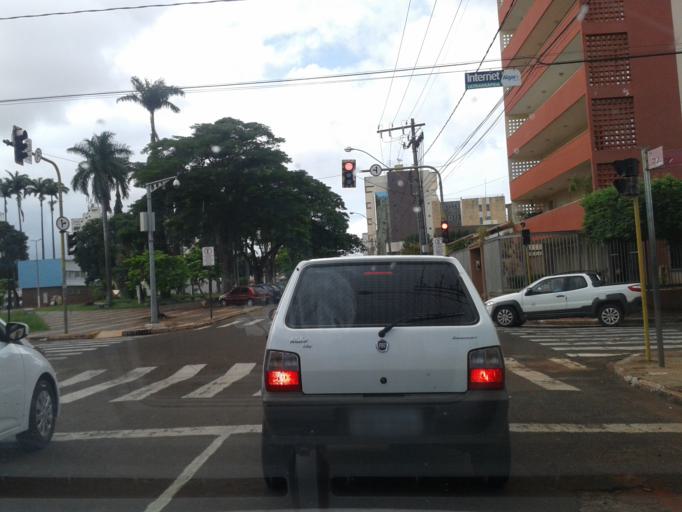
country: BR
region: Minas Gerais
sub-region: Ituiutaba
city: Ituiutaba
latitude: -18.9693
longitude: -49.4647
